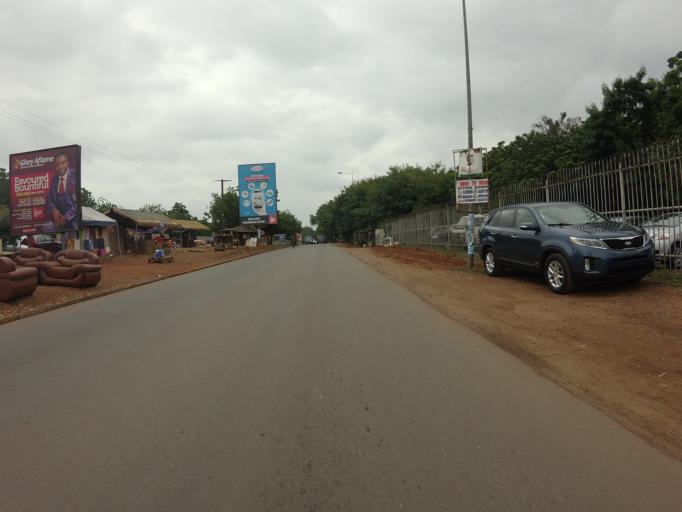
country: GH
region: Greater Accra
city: Dome
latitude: 5.6343
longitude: -0.2157
